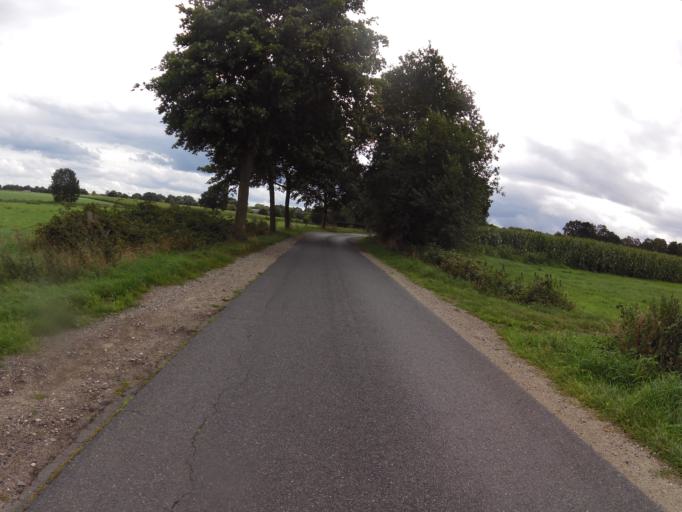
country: DE
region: Lower Saxony
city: Loxstedt
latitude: 53.4994
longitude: 8.7041
